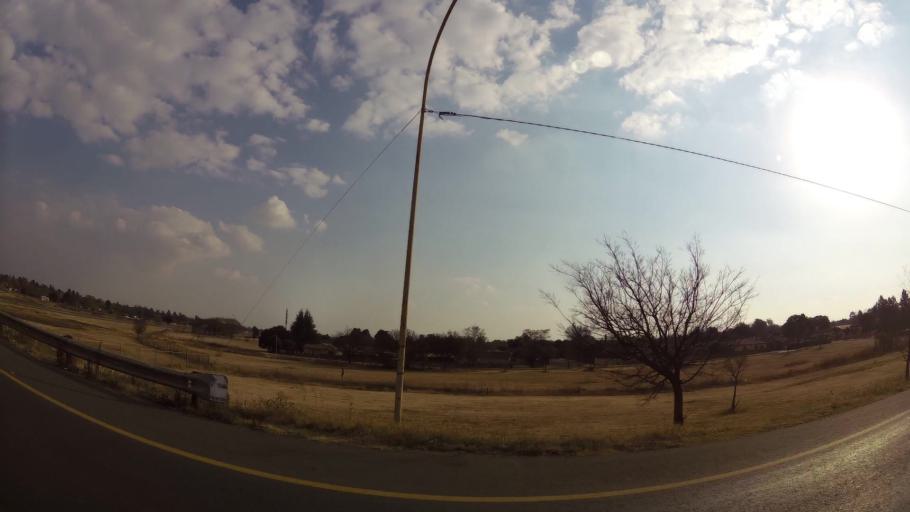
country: ZA
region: Gauteng
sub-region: Ekurhuleni Metropolitan Municipality
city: Springs
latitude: -26.2779
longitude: 28.4527
